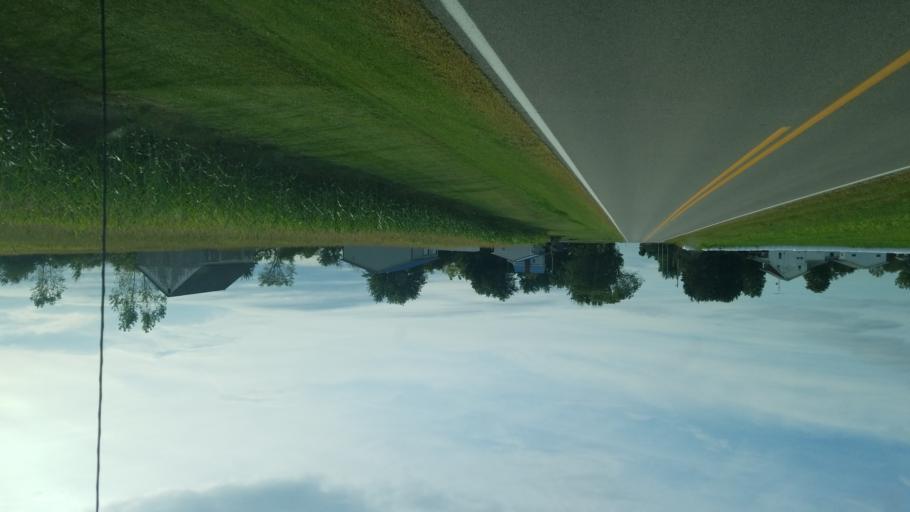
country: US
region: Ohio
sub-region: Crawford County
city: Bucyrus
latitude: 40.8985
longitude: -83.0935
